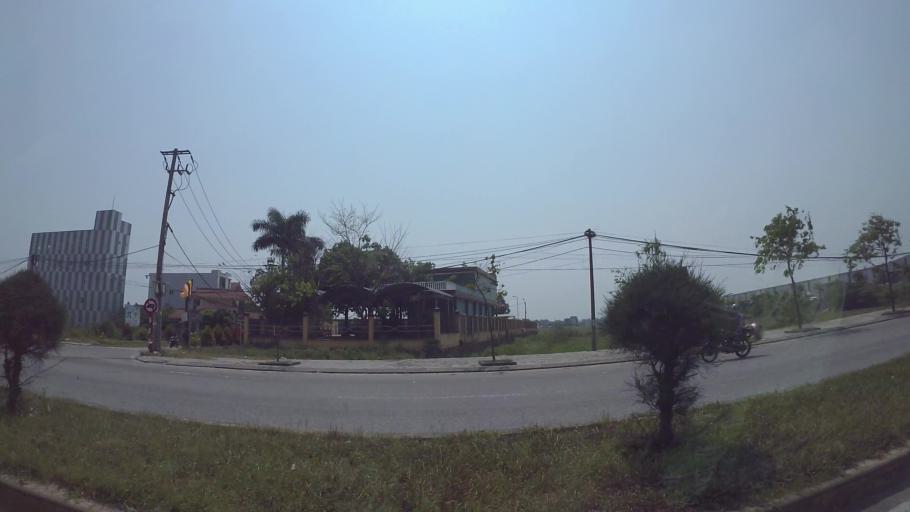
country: VN
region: Da Nang
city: Cam Le
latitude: 15.9840
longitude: 108.2040
